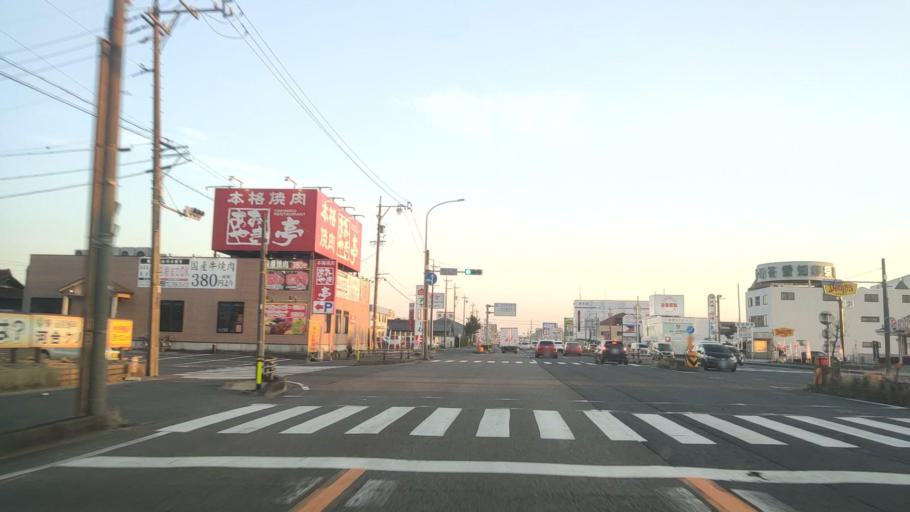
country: JP
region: Aichi
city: Ichinomiya
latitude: 35.3091
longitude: 136.8195
